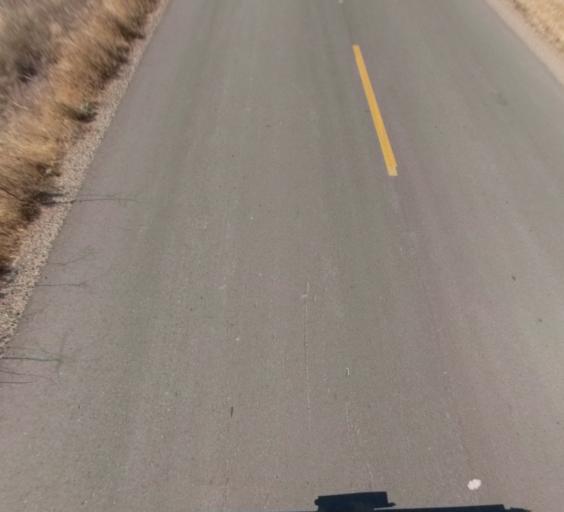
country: US
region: California
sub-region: Madera County
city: Bonadelle Ranchos-Madera Ranchos
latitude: 36.9854
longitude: -119.8829
